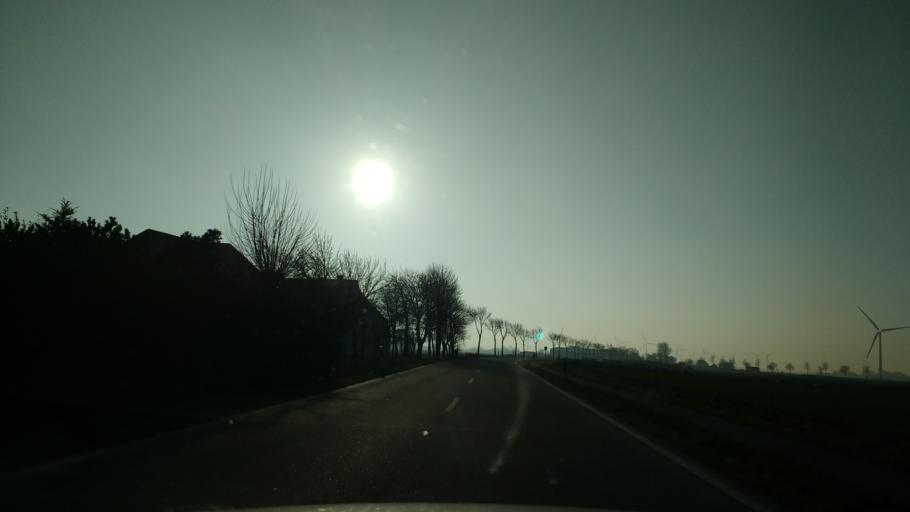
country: DE
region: Schleswig-Holstein
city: Helse
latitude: 53.9887
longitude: 8.9943
